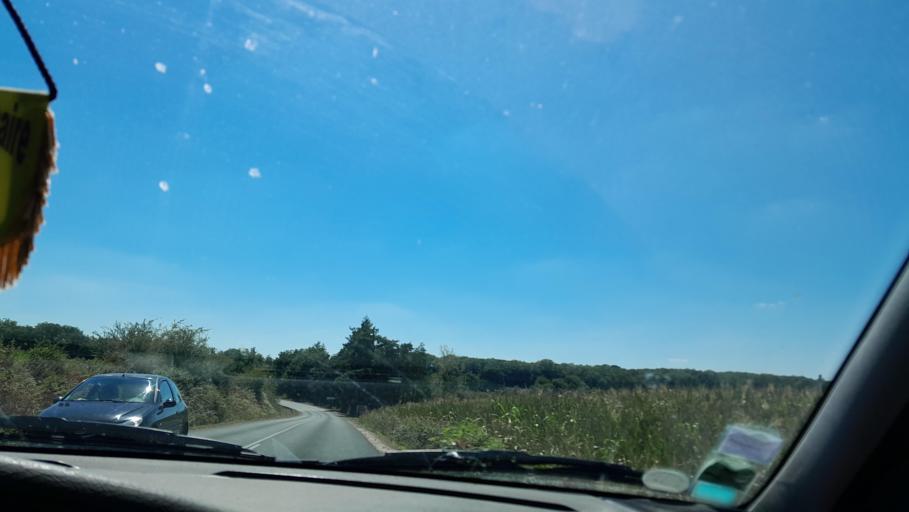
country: FR
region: Pays de la Loire
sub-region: Departement de Maine-et-Loire
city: Pouance
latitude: 47.6999
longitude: -1.1820
